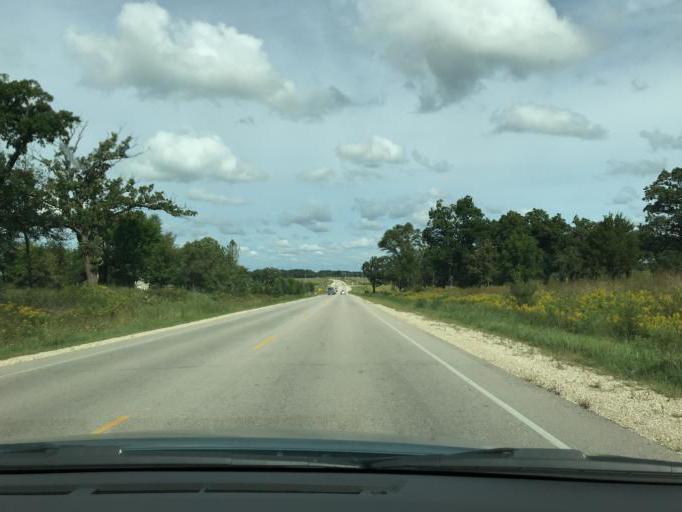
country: US
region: Wisconsin
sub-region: Racine County
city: Bohners Lake
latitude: 42.6065
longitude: -88.2264
